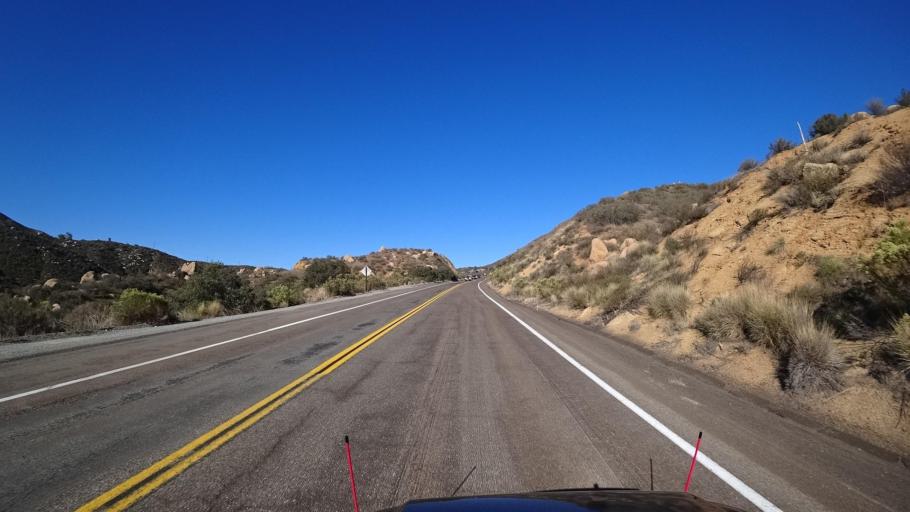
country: MX
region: Baja California
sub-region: Tecate
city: Lomas de Santa Anita
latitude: 32.6154
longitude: -116.7236
